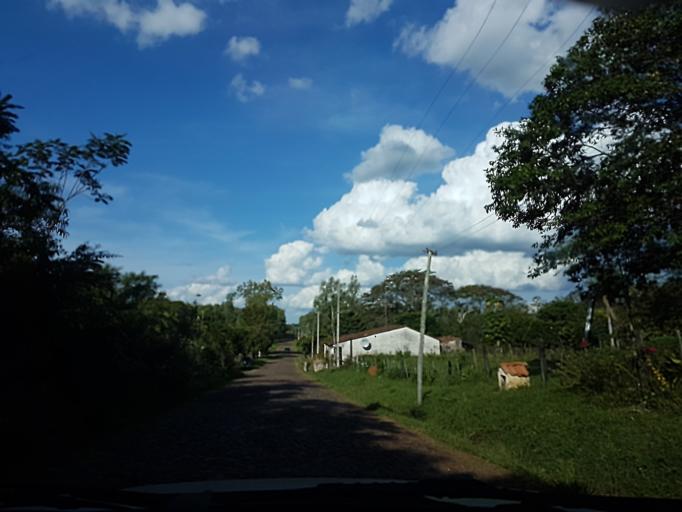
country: PY
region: Cordillera
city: Arroyos y Esteros
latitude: -24.9967
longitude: -57.1533
